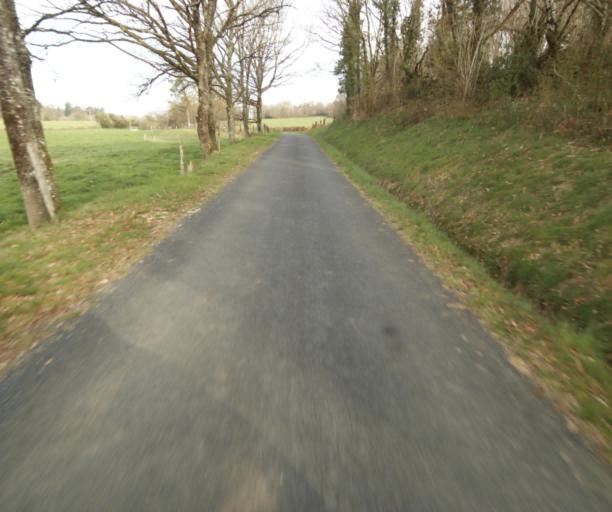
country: FR
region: Limousin
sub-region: Departement de la Correze
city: Chamboulive
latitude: 45.4481
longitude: 1.7547
